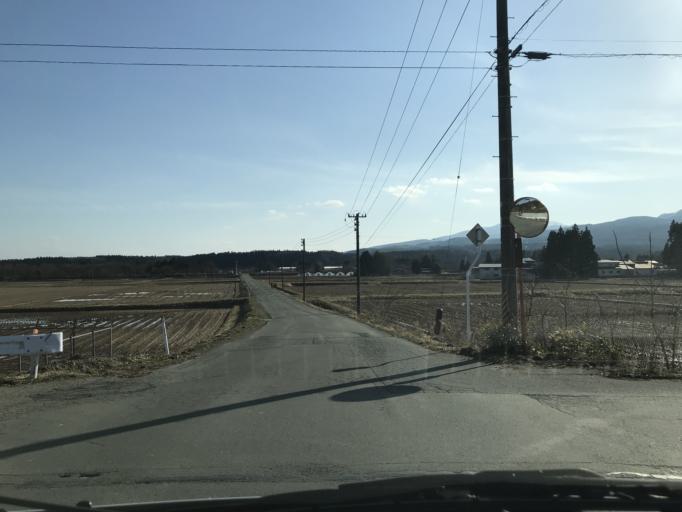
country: JP
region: Iwate
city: Kitakami
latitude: 39.2994
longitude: 141.0046
